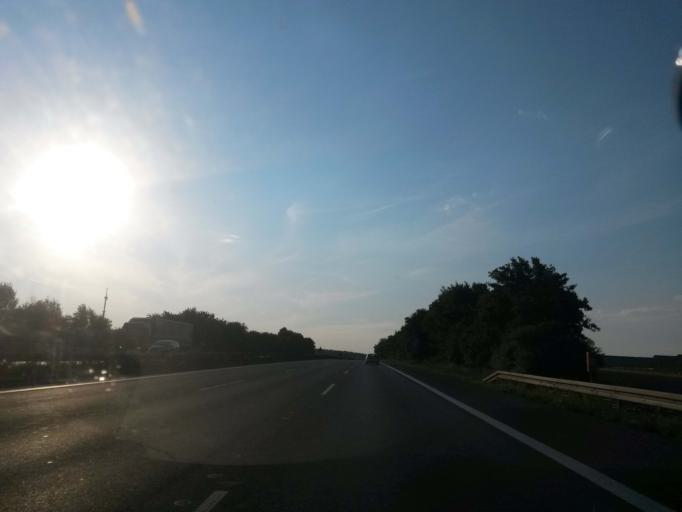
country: DE
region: Bavaria
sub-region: Upper Bavaria
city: Denkendorf
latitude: 48.9424
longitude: 11.4470
